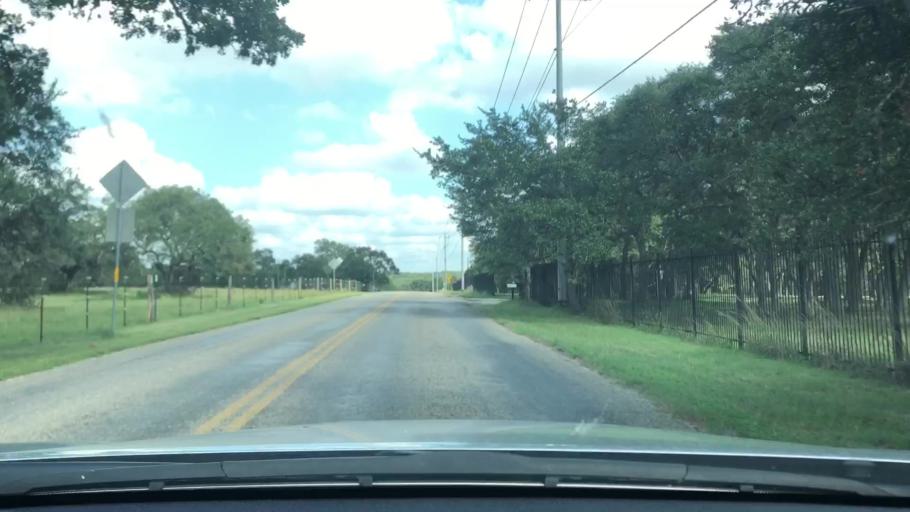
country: US
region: Texas
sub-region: Bexar County
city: Fair Oaks Ranch
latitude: 29.7851
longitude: -98.6302
